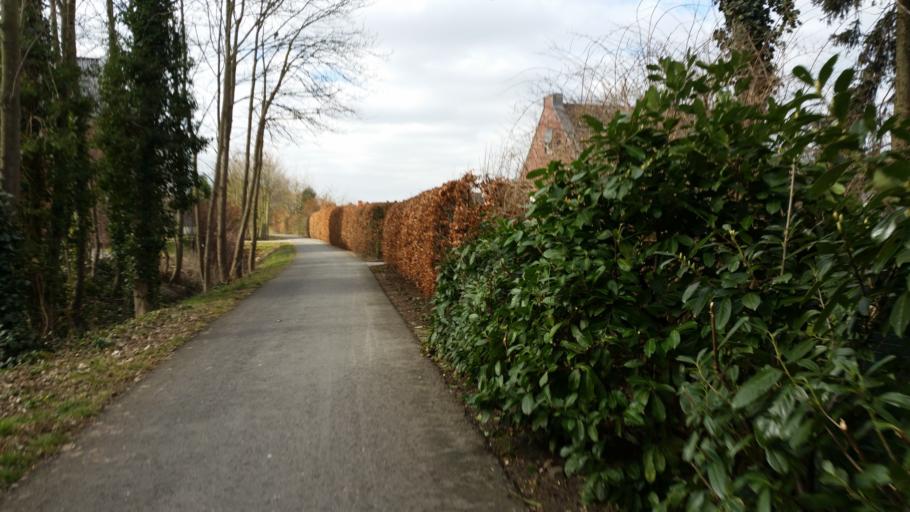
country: DE
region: North Rhine-Westphalia
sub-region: Regierungsbezirk Munster
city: Rheine
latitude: 52.2818
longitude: 7.4210
